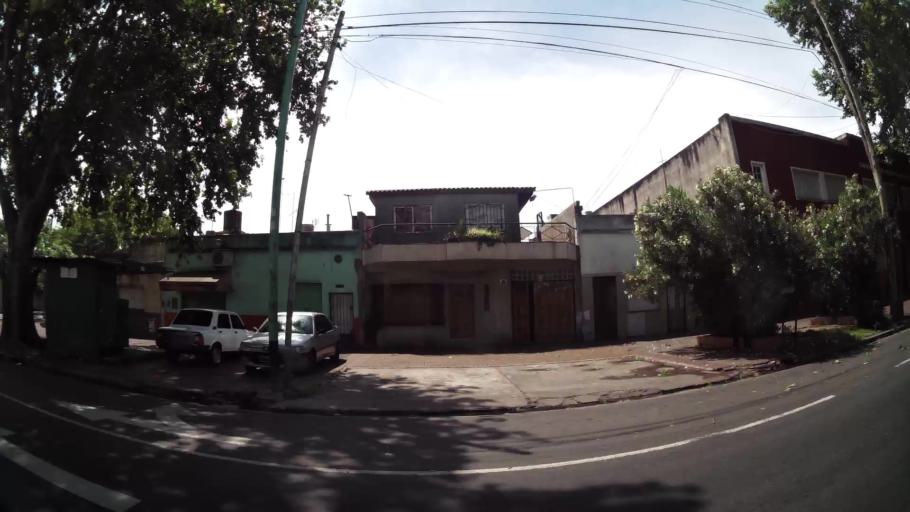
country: AR
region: Buenos Aires F.D.
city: Villa Lugano
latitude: -34.6623
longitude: -58.4346
